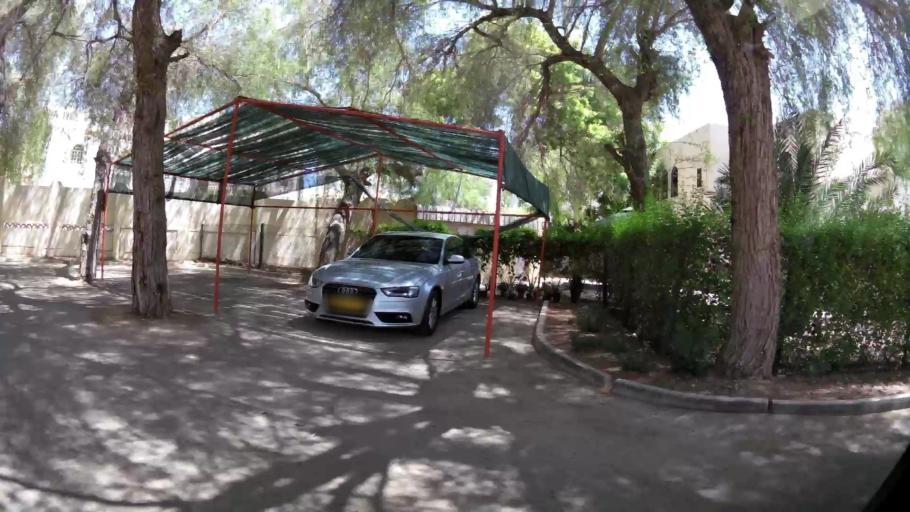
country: OM
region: Muhafazat Masqat
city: Bawshar
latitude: 23.5905
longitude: 58.3976
